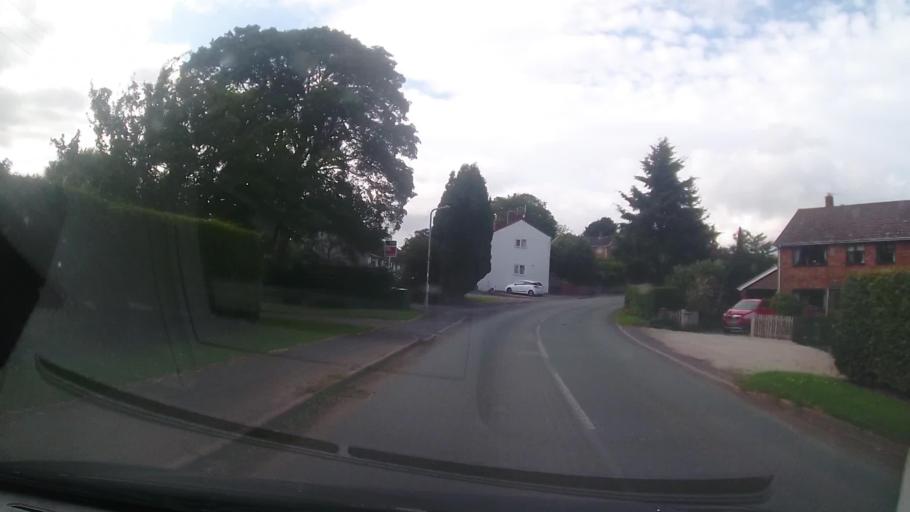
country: GB
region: England
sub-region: Shropshire
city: Great Hanwood
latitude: 52.6513
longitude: -2.8267
